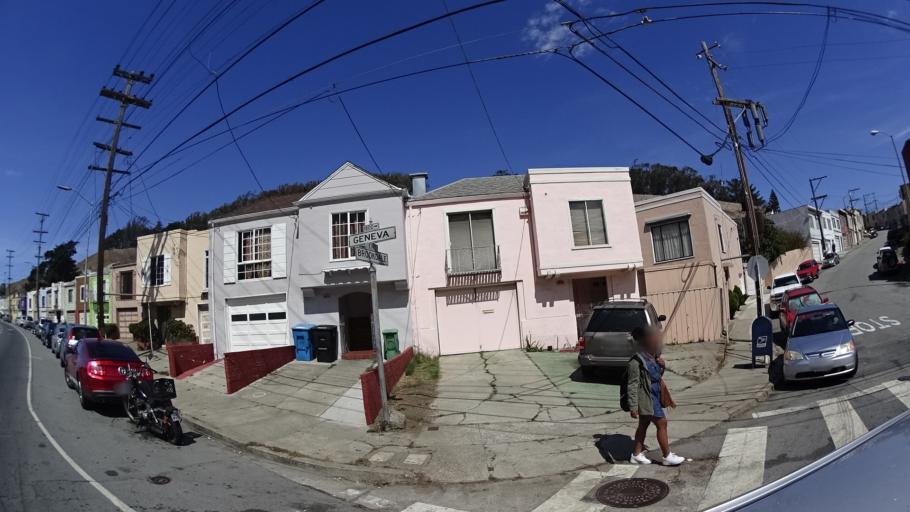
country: US
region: California
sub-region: San Mateo County
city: Daly City
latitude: 37.7102
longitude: -122.4244
